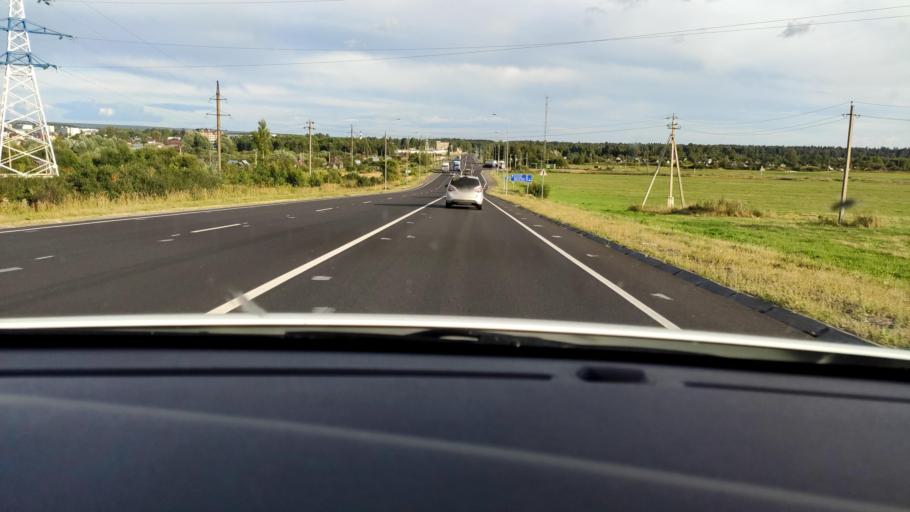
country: RU
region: Mariy-El
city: Krasnogorskiy
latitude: 56.1710
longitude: 48.2800
